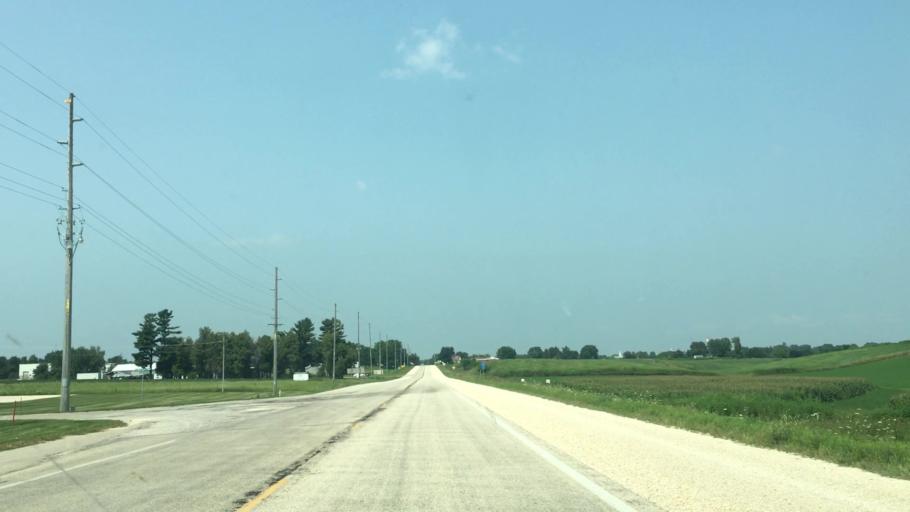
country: US
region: Iowa
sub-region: Fayette County
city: West Union
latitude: 42.9430
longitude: -91.8142
